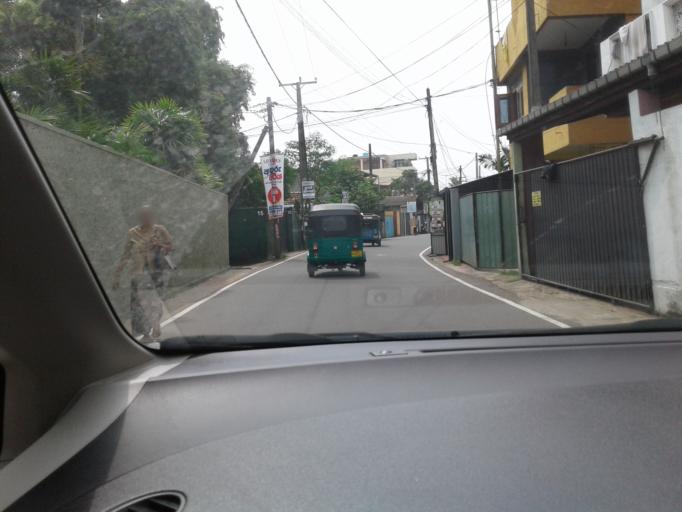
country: LK
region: Western
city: Maharagama
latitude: 6.8506
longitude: 79.9208
